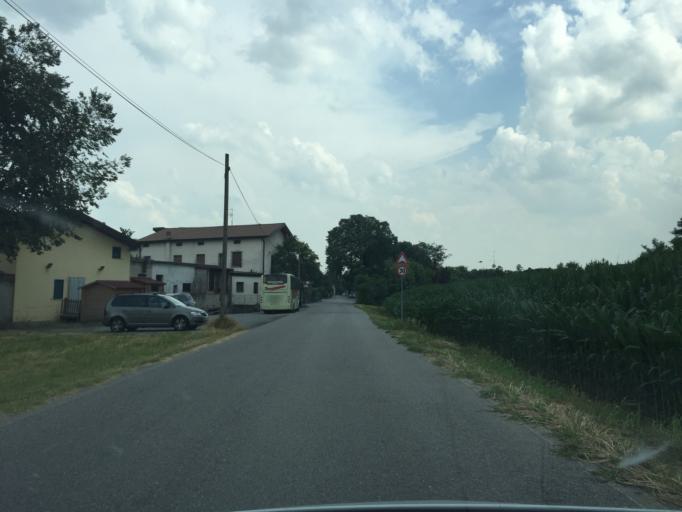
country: IT
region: Lombardy
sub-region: Provincia di Brescia
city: Flero
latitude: 45.4897
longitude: 10.1754
